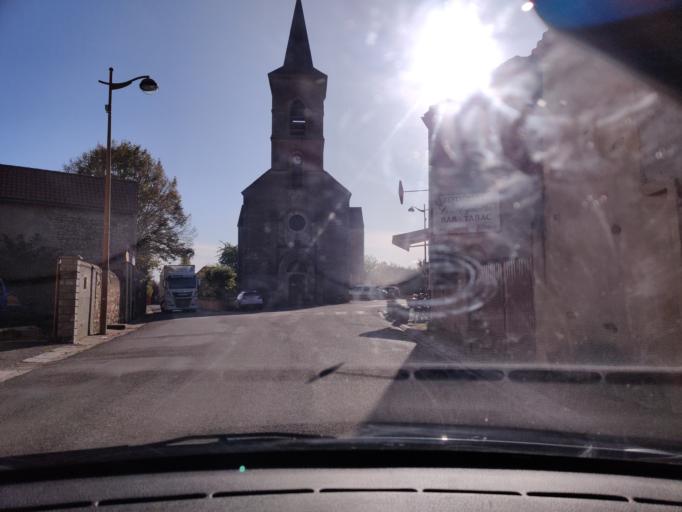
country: FR
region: Auvergne
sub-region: Departement du Puy-de-Dome
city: Aigueperse
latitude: 46.0409
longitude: 3.1358
